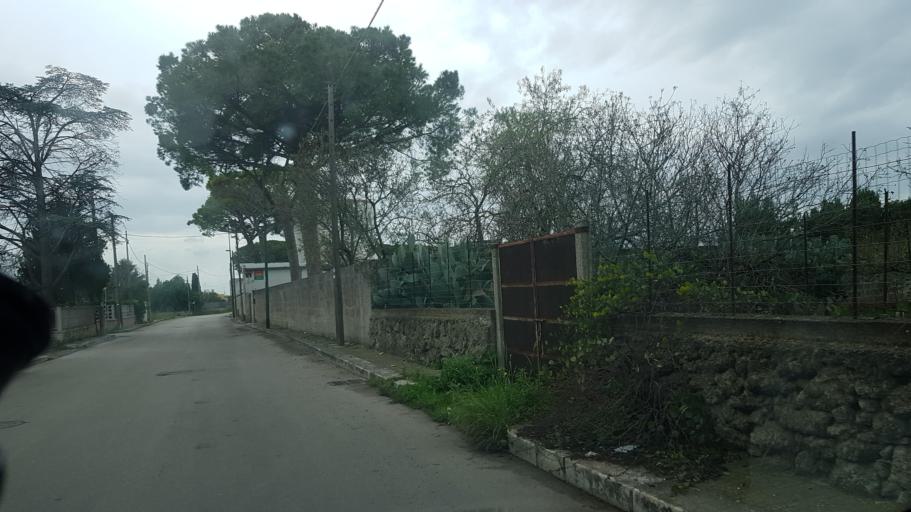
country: IT
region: Apulia
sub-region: Provincia di Lecce
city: Campi Salentina
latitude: 40.3920
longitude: 18.0189
